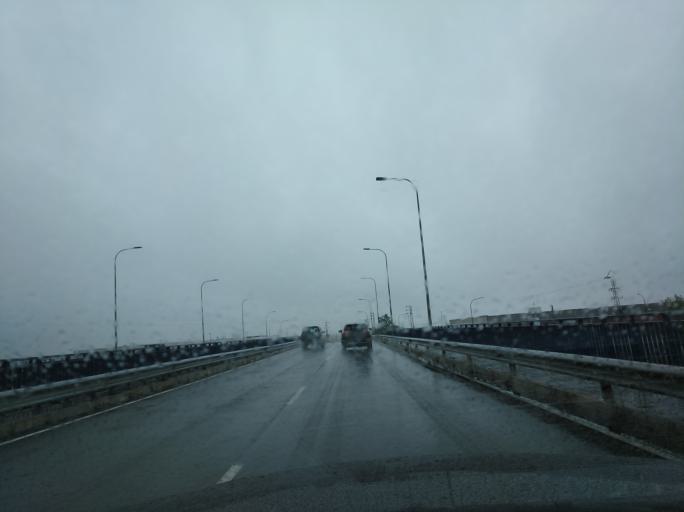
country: ES
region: Extremadura
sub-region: Provincia de Badajoz
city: Badajoz
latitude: 38.8971
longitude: -6.9915
